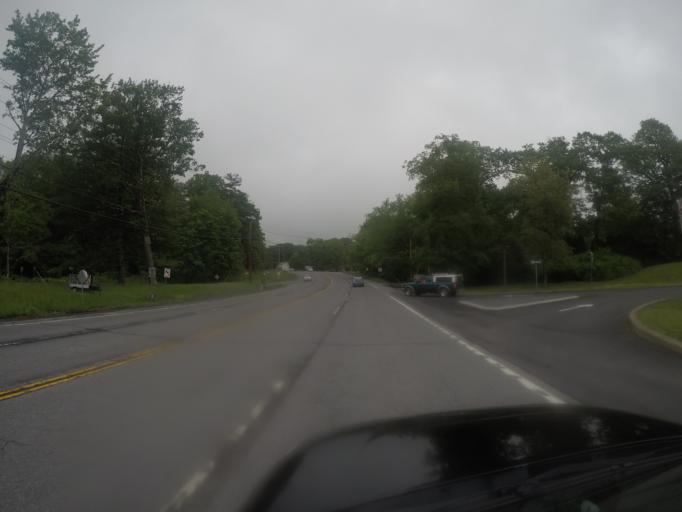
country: US
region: New York
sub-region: Ulster County
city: West Hurley
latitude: 41.9938
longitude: -74.0878
